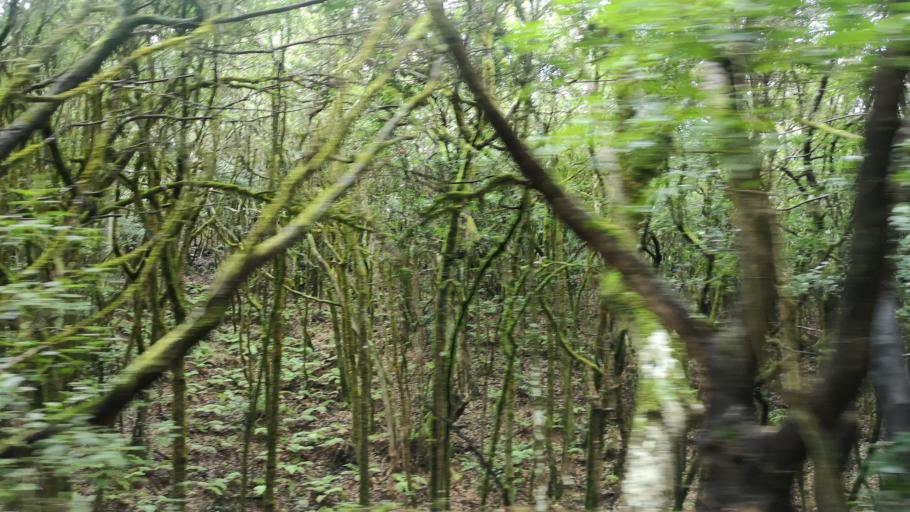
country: ES
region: Canary Islands
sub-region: Provincia de Santa Cruz de Tenerife
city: Vallehermosa
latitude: 28.1597
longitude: -17.2979
